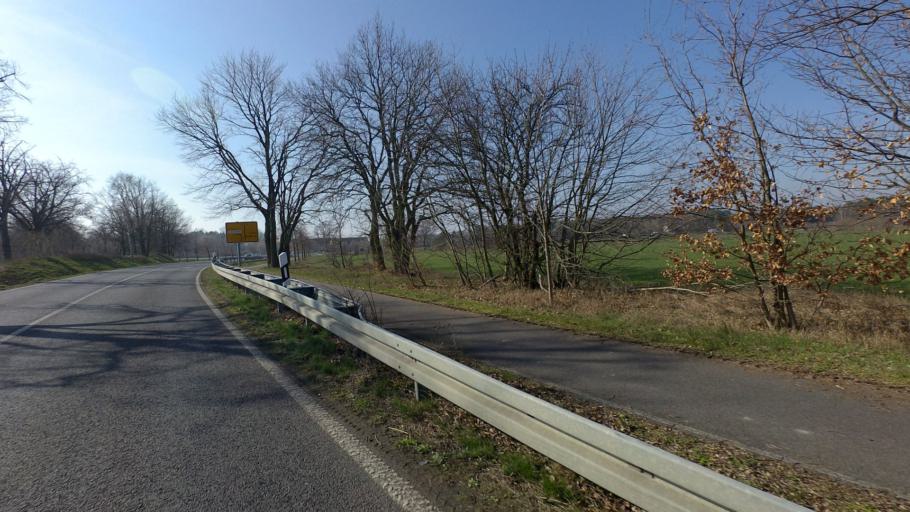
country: DE
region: Berlin
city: Lichtenrade
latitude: 52.3665
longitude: 13.4417
